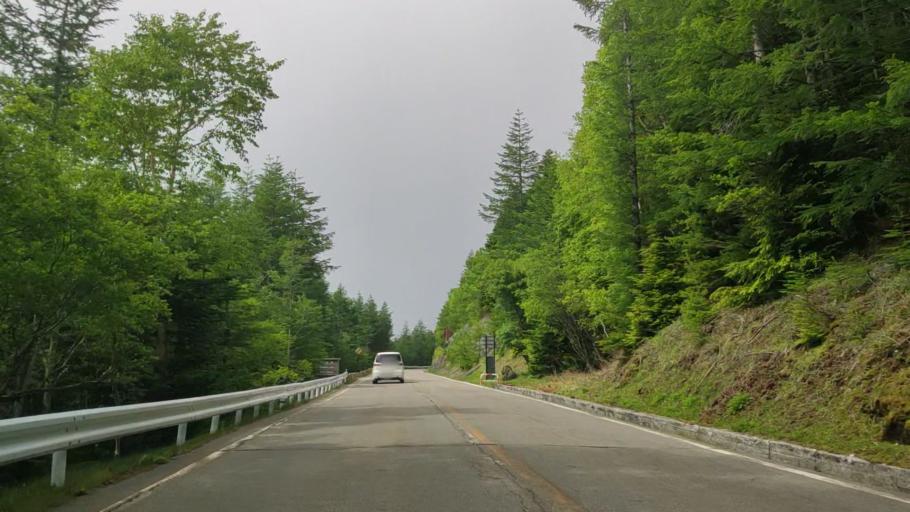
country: JP
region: Yamanashi
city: Fujikawaguchiko
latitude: 35.3781
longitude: 138.6931
